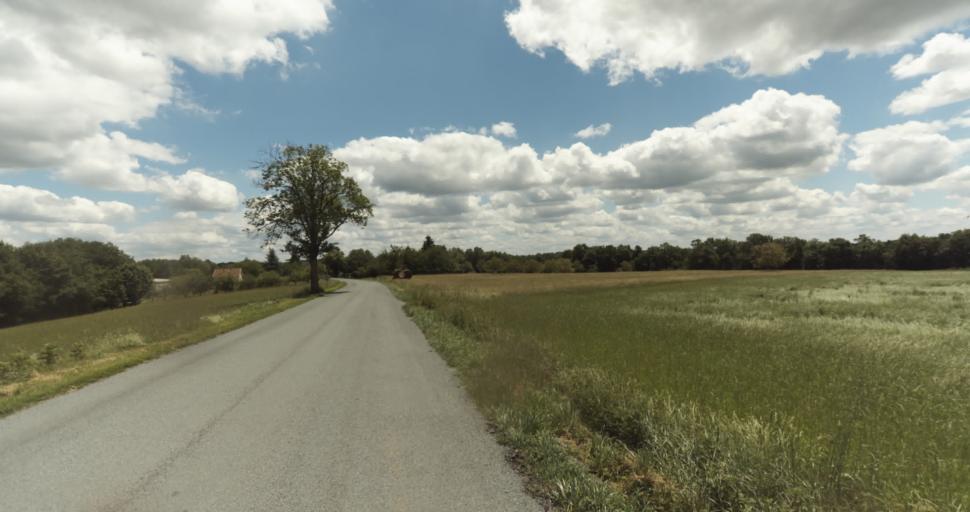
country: FR
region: Aquitaine
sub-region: Departement de la Dordogne
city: Beaumont-du-Perigord
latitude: 44.7041
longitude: 0.8345
